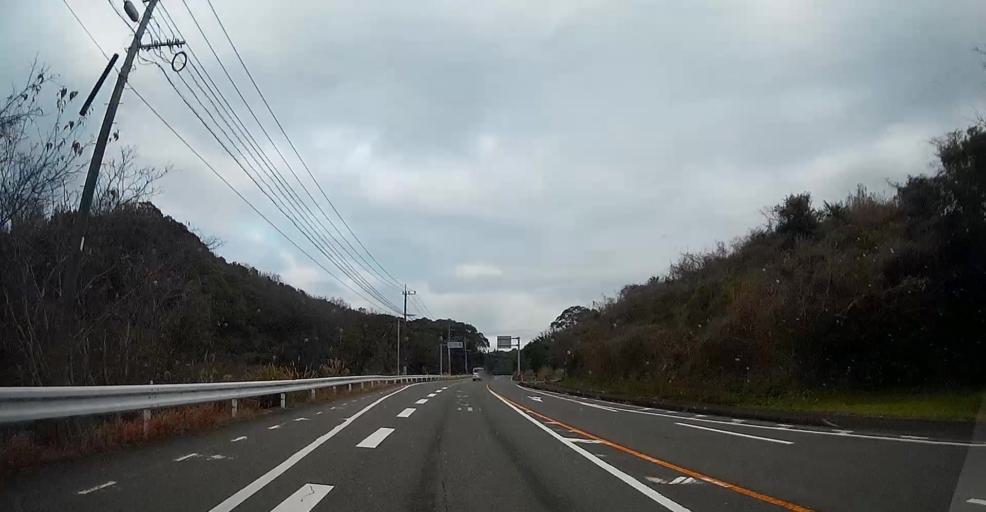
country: JP
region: Kumamoto
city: Hondo
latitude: 32.4933
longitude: 130.2958
